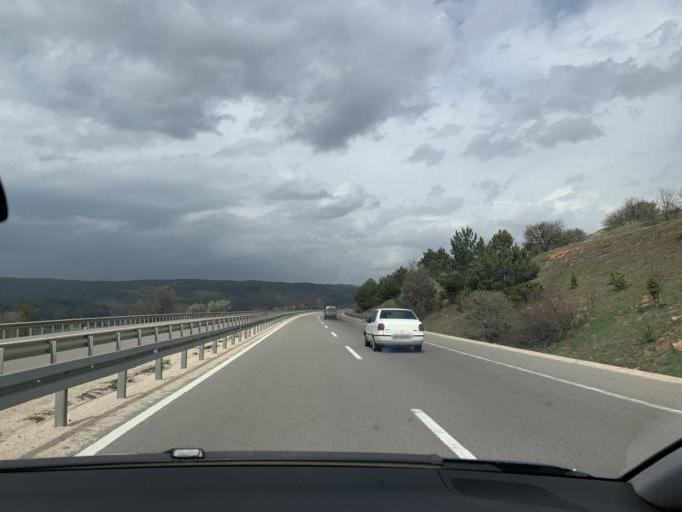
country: TR
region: Bolu
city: Yenicaga
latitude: 40.7840
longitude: 32.1055
